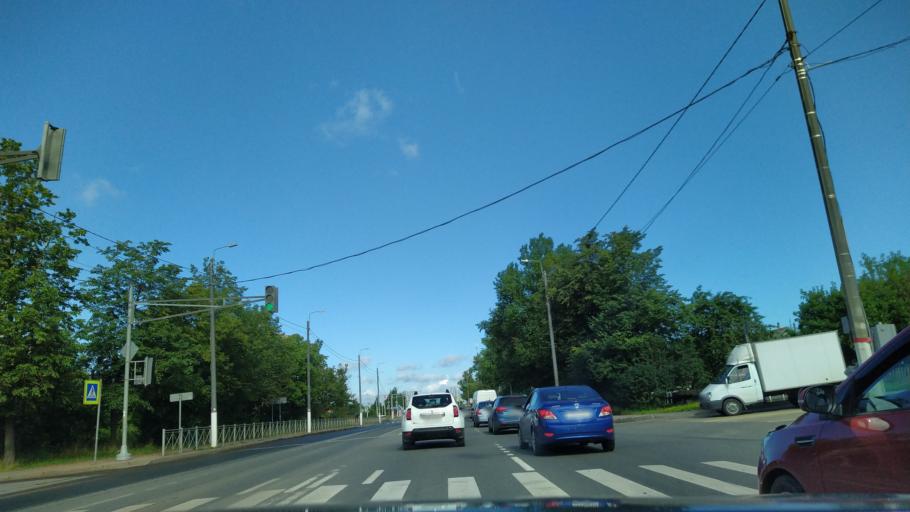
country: RU
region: Leningrad
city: Tosno
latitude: 59.5478
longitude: 30.8647
